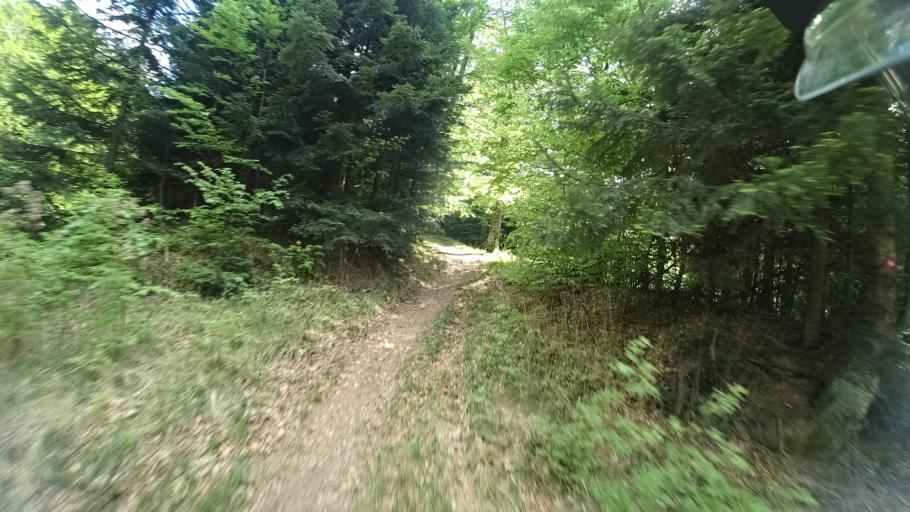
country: HR
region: Grad Zagreb
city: Kasina
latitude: 45.9205
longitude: 15.9449
